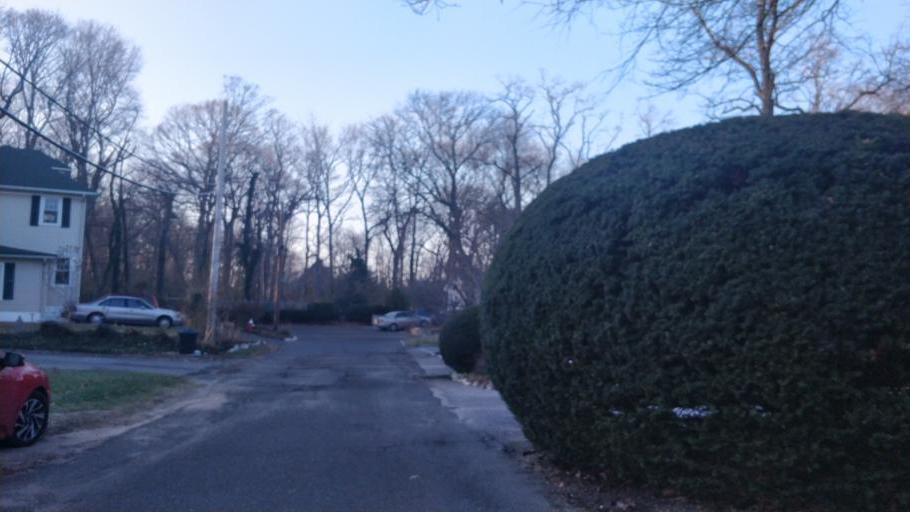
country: US
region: New York
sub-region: Nassau County
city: Bayville
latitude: 40.9112
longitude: -73.5588
